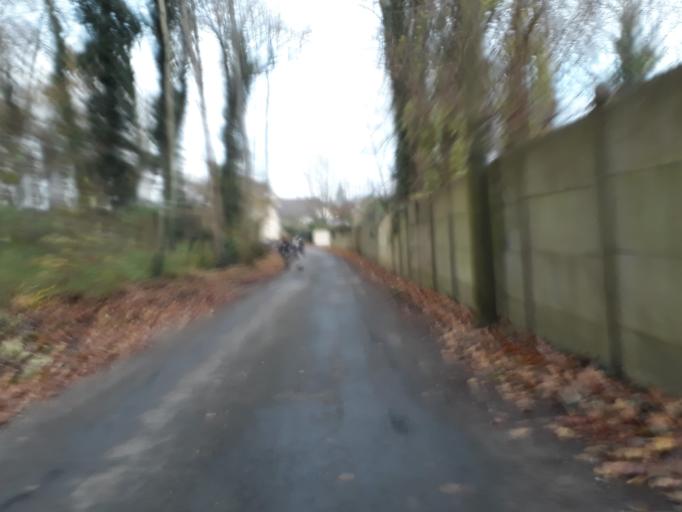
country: FR
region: Ile-de-France
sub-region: Departement de Seine-et-Marne
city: Chartrettes
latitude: 48.4793
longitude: 2.6791
